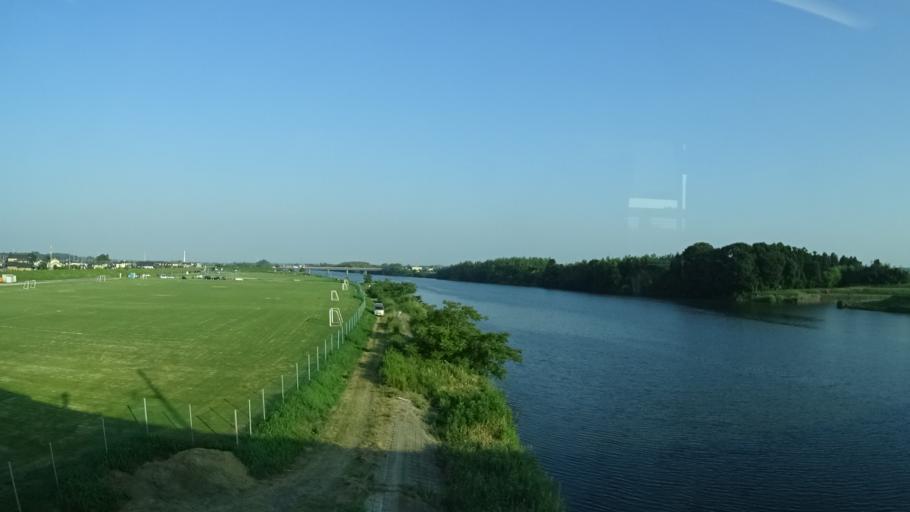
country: JP
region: Ibaraki
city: Katsuta
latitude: 36.3759
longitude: 140.5107
